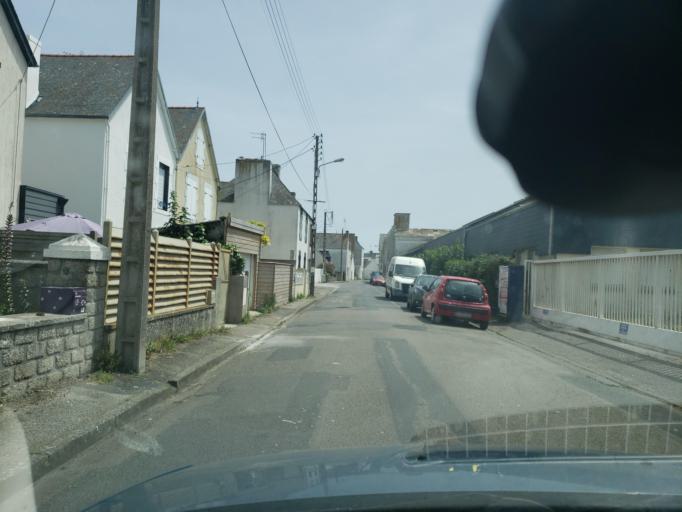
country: FR
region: Brittany
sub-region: Departement du Finistere
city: Guilvinec
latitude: 47.7988
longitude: -4.2836
